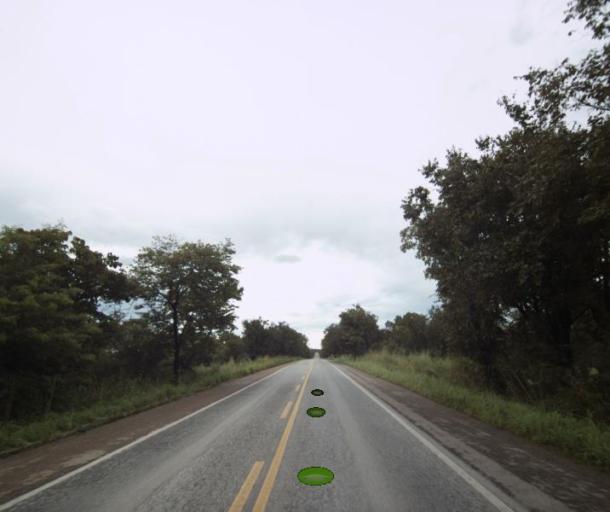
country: BR
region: Goias
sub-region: Porangatu
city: Porangatu
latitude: -13.6681
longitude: -49.0298
